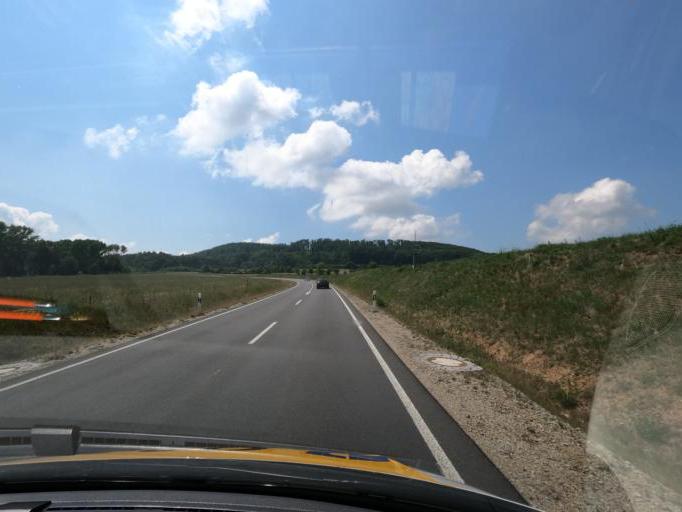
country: DE
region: Thuringia
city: Buhla
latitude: 51.4413
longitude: 10.4470
